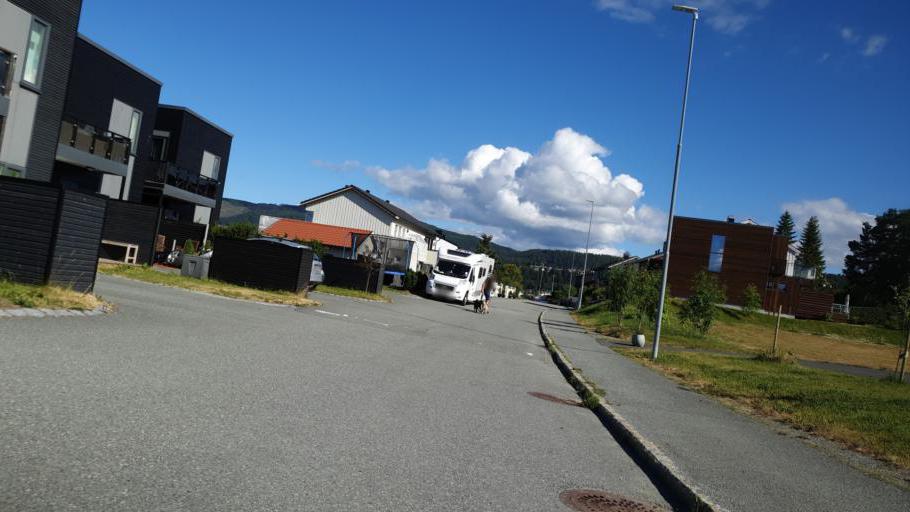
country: NO
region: Sor-Trondelag
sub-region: Trondheim
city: Trondheim
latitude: 63.4288
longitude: 10.5075
